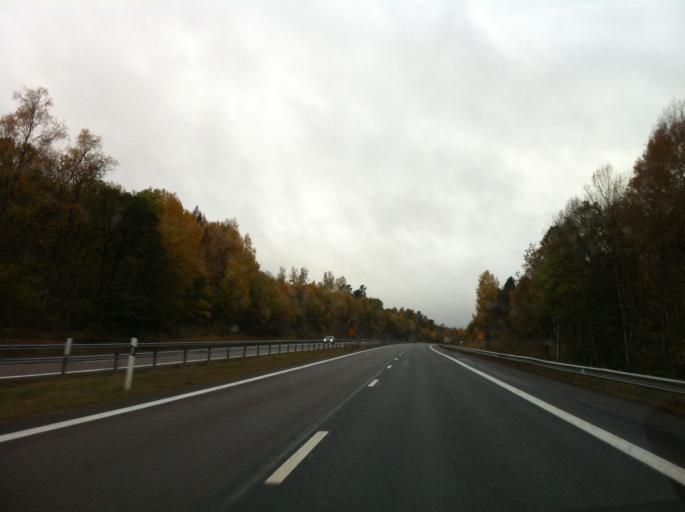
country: SE
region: Joenkoeping
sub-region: Jonkopings Kommun
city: Graenna
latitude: 58.0208
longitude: 14.4775
